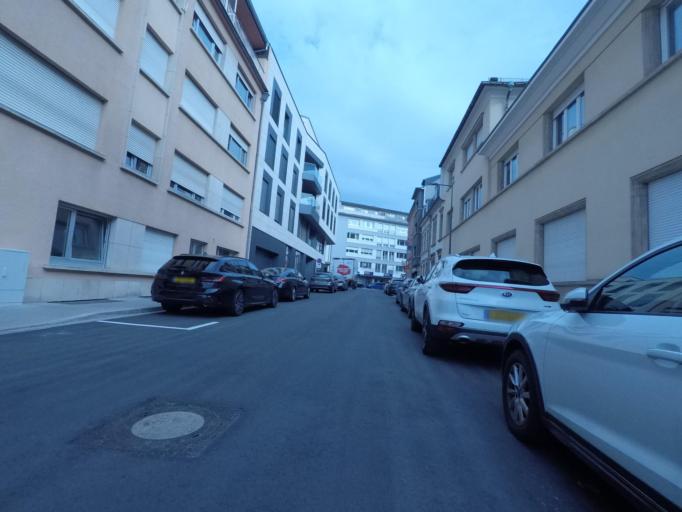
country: LU
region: Luxembourg
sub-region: Canton de Luxembourg
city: Luxembourg
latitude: 49.6086
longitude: 6.1185
